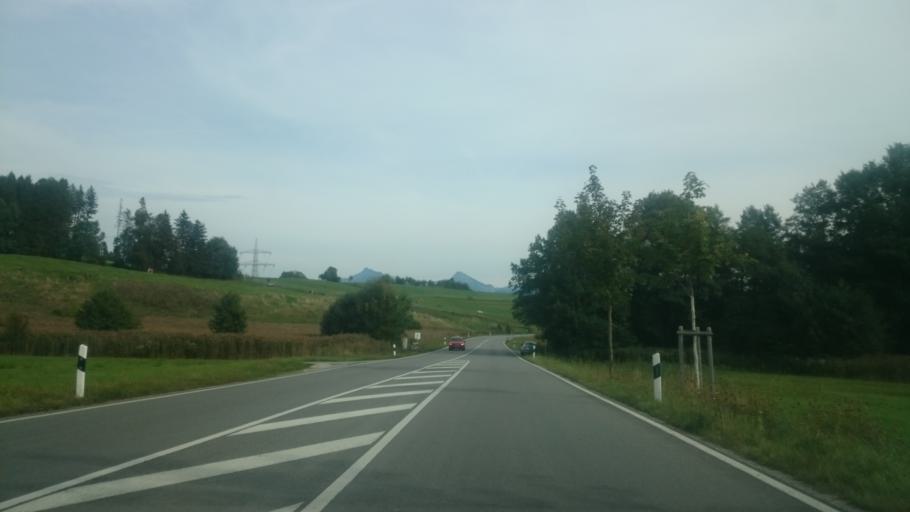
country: AT
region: Tyrol
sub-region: Politischer Bezirk Reutte
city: Vils
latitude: 47.5769
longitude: 10.6307
